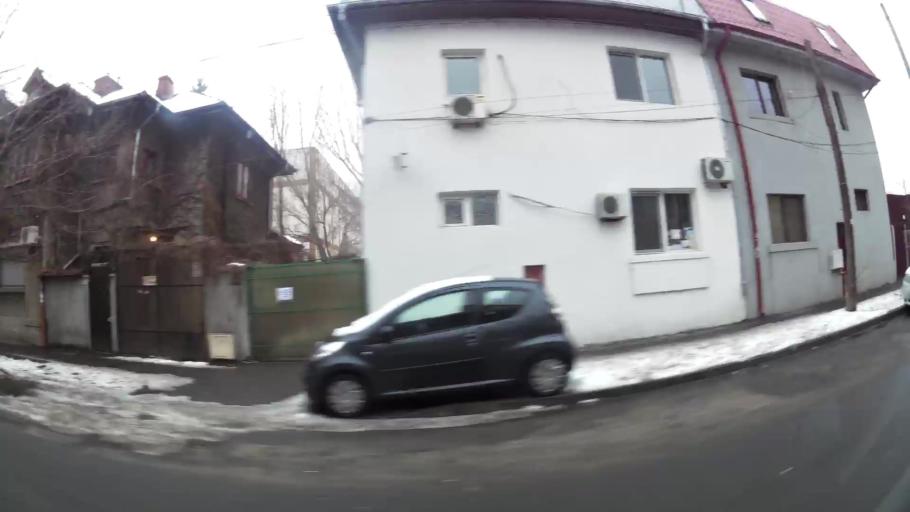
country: RO
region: Ilfov
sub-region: Comuna Chiajna
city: Rosu
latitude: 44.4503
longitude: 26.0550
